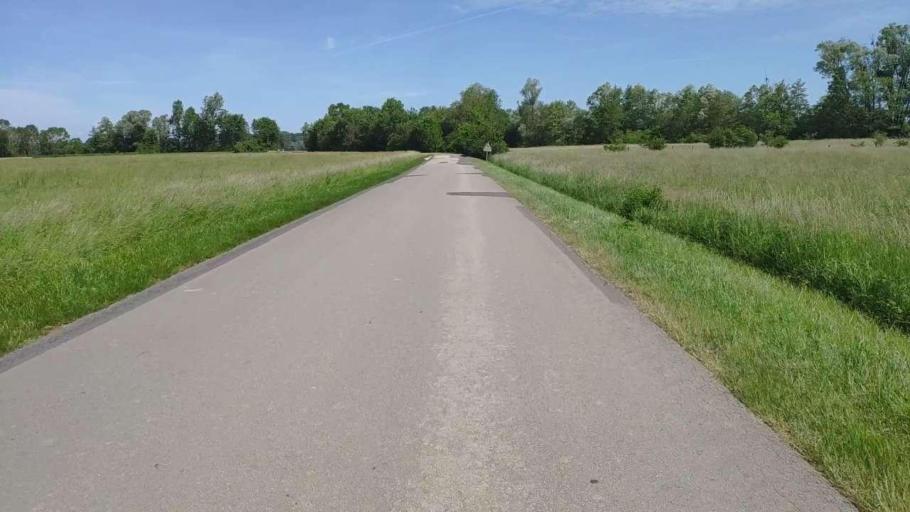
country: FR
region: Franche-Comte
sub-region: Departement du Jura
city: Bletterans
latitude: 46.7231
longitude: 5.4448
